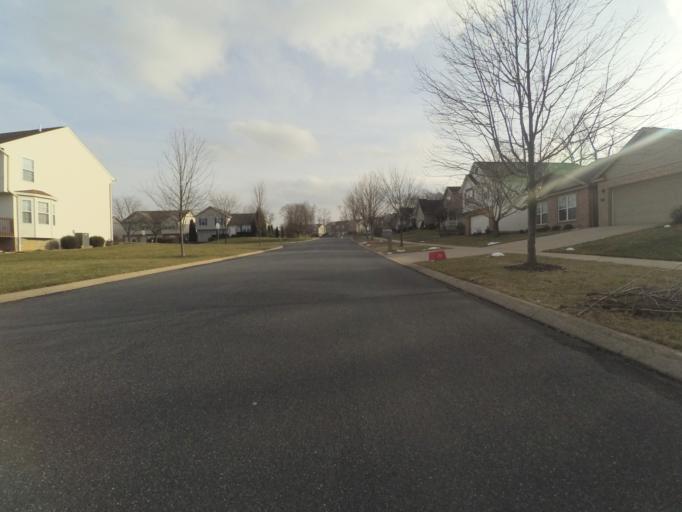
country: US
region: Pennsylvania
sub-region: Centre County
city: Park Forest Village
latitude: 40.7850
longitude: -77.8987
